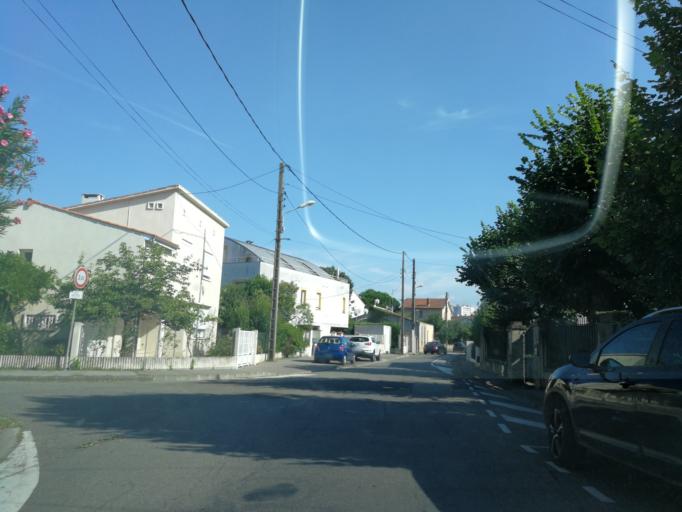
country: FR
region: Midi-Pyrenees
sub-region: Departement de la Haute-Garonne
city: Toulouse
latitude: 43.6270
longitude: 1.4259
